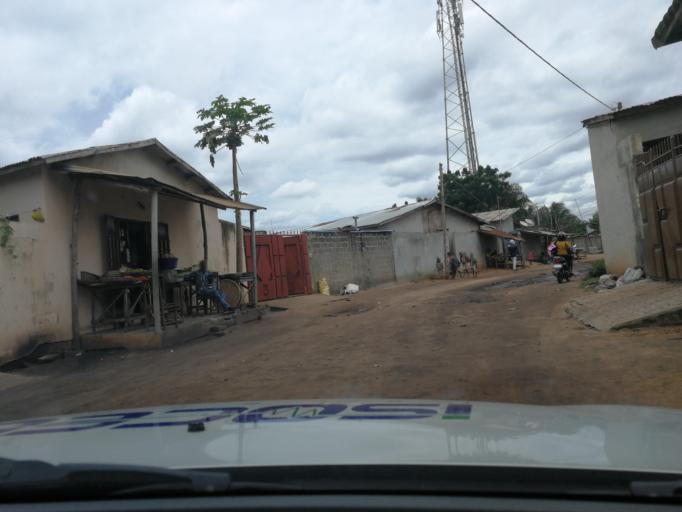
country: BJ
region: Atlantique
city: Abomey-Calavi
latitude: 6.4382
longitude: 2.3054
